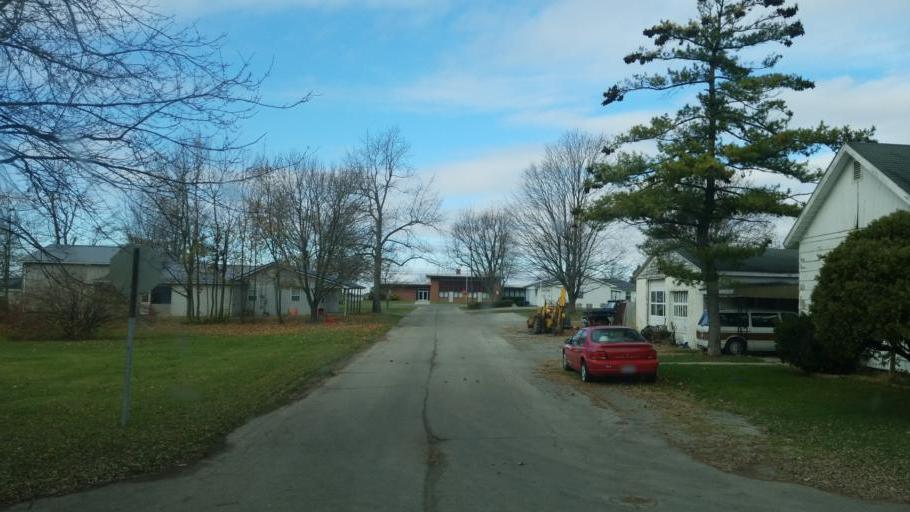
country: US
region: Ohio
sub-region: Hardin County
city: Kenton
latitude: 40.6527
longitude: -83.6196
